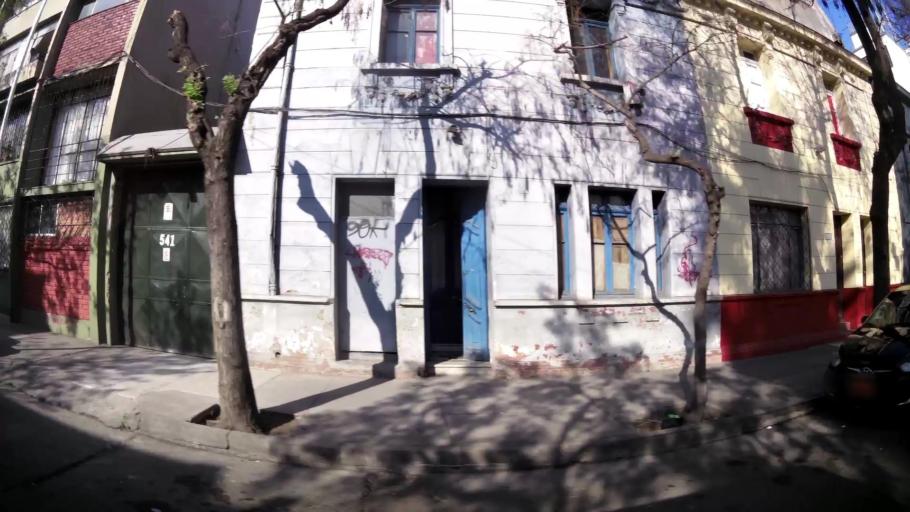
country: CL
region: Santiago Metropolitan
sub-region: Provincia de Santiago
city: Santiago
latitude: -33.4393
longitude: -70.6767
